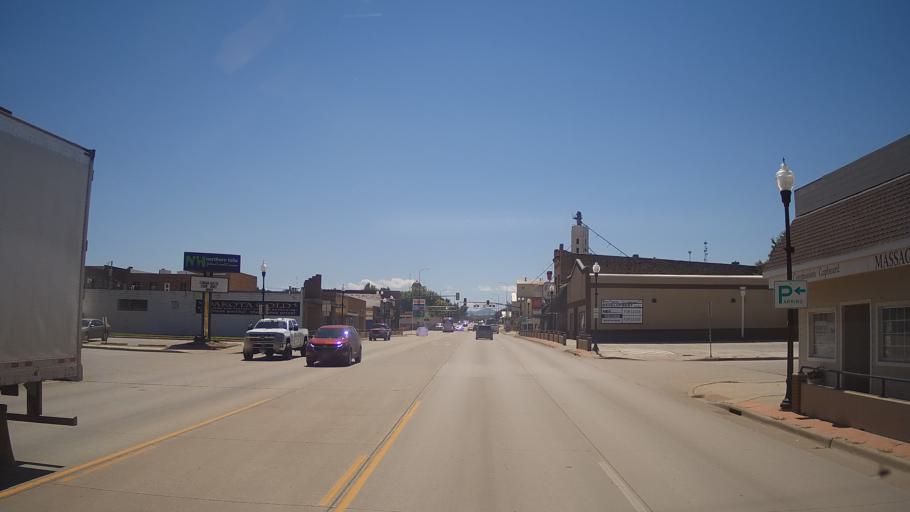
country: US
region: South Dakota
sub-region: Butte County
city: Belle Fourche
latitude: 44.6729
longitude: -103.8536
